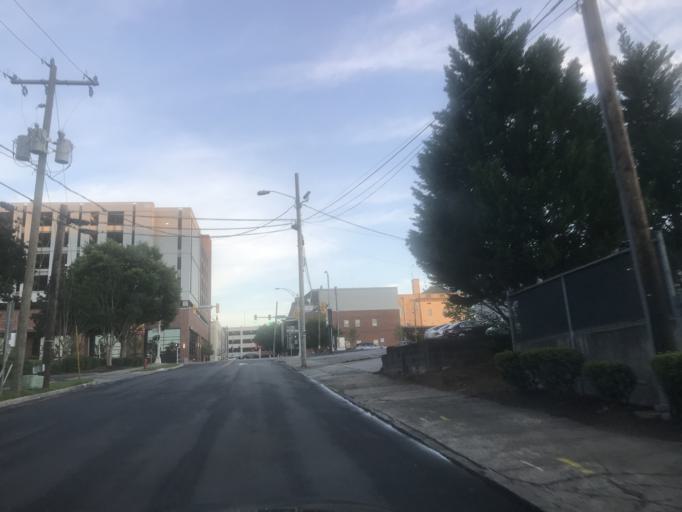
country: US
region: North Carolina
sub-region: Durham County
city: Durham
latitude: 35.9987
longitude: -78.9000
